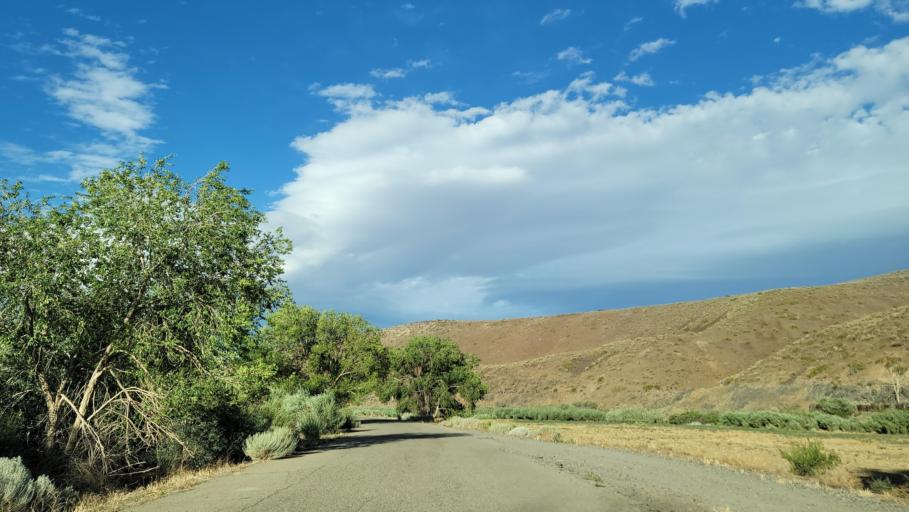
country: US
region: Nevada
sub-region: Washoe County
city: Sparks
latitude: 39.5106
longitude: -119.6239
